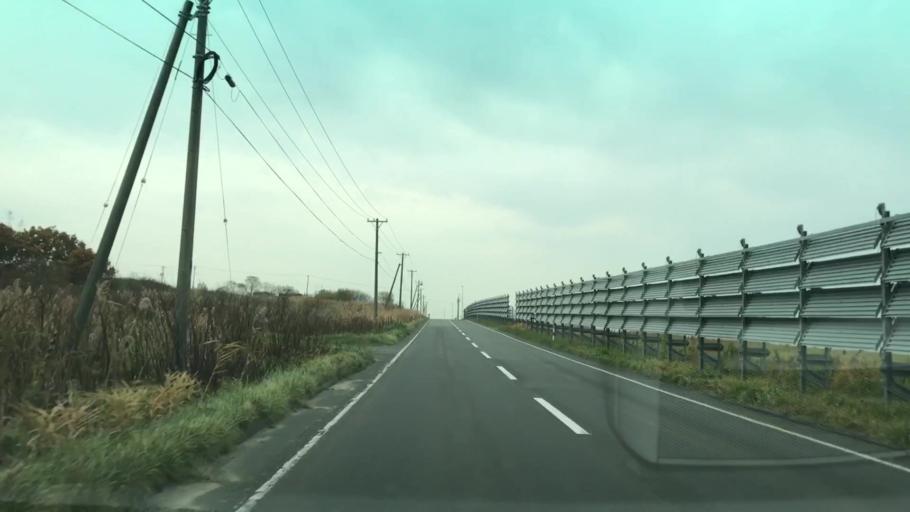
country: JP
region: Hokkaido
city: Ishikari
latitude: 43.3468
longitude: 141.4243
